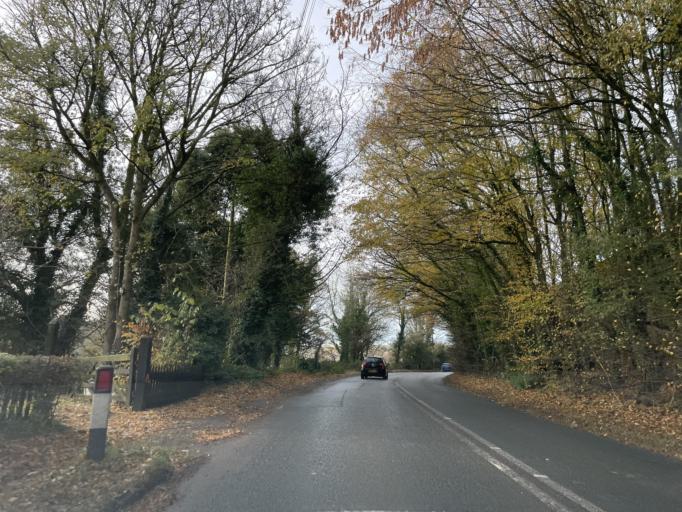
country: GB
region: England
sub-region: Borough of Swindon
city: Wroughton
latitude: 51.5206
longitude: -1.8016
